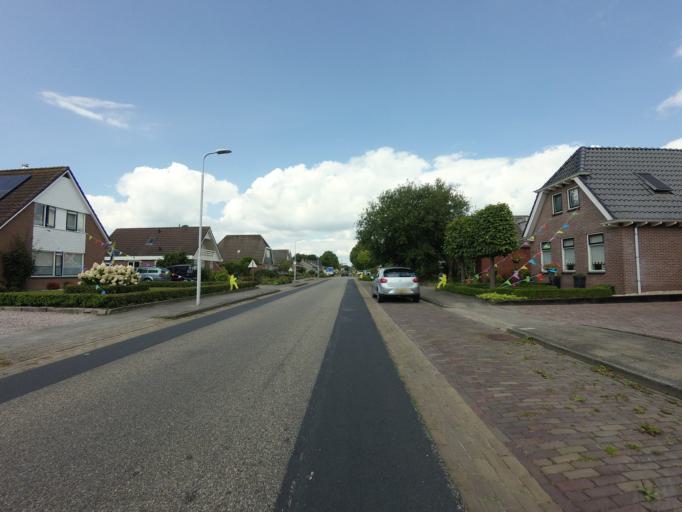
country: NL
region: Friesland
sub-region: Gemeente Heerenveen
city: Jubbega
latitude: 52.9779
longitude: 6.2181
